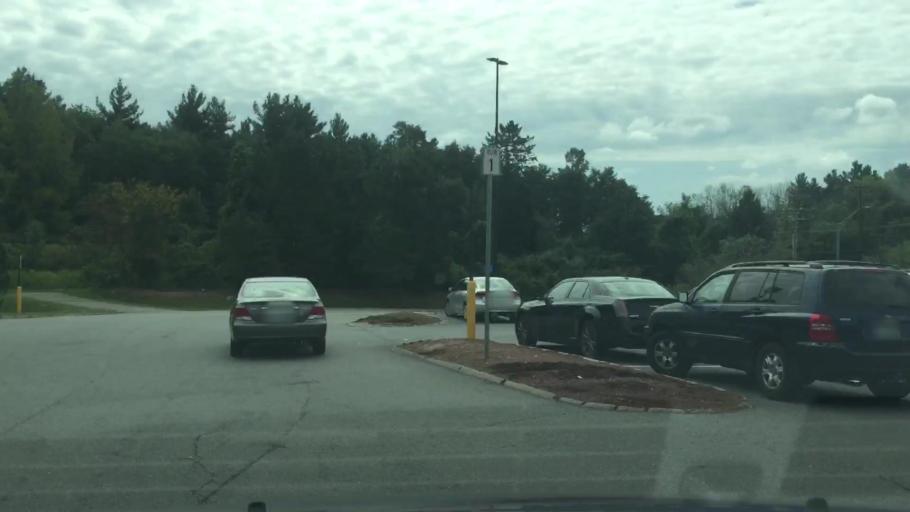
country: US
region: New Hampshire
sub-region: Hillsborough County
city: Hudson
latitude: 42.7269
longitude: -71.4231
